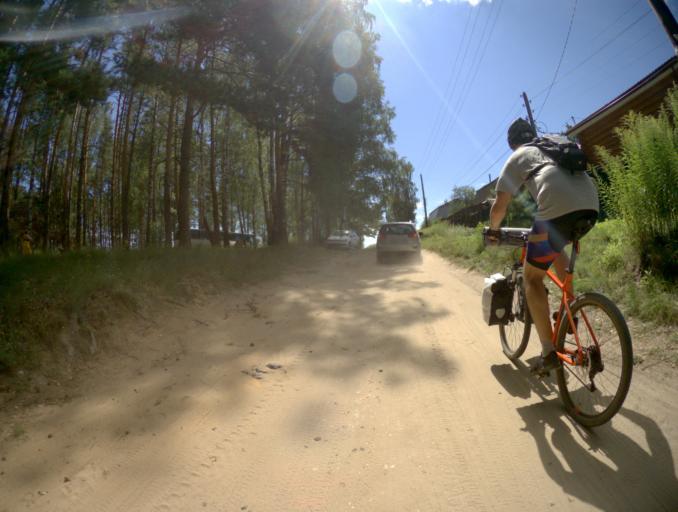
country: RU
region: Nizjnij Novgorod
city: Neklyudovo
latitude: 56.4541
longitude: 44.0059
